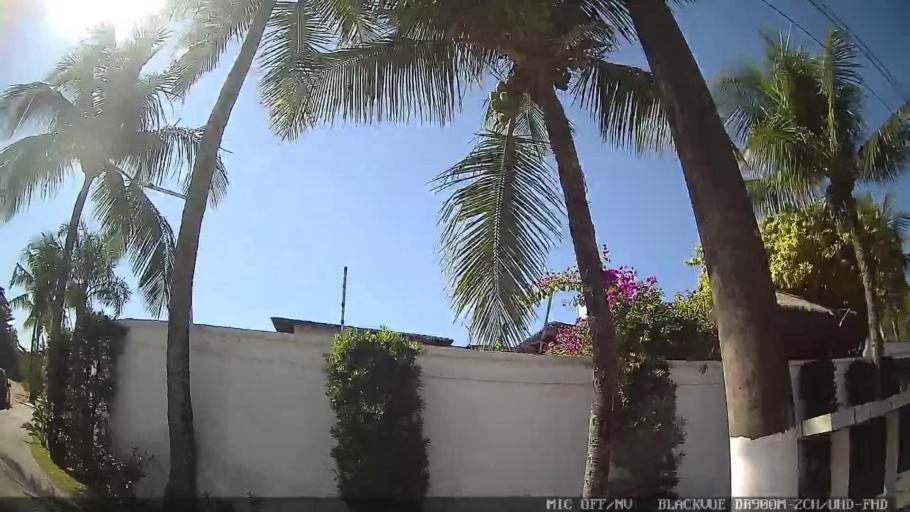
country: BR
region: Sao Paulo
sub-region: Guaruja
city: Guaruja
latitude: -23.9817
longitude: -46.2151
